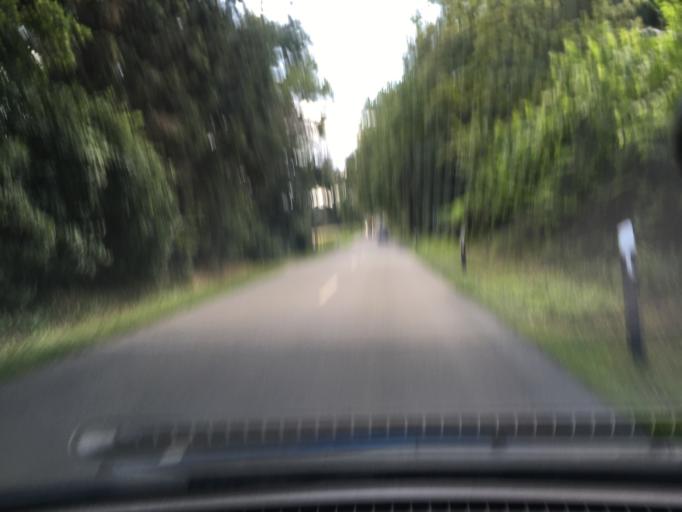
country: DE
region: Lower Saxony
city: Vastorf
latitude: 53.1792
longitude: 10.5239
